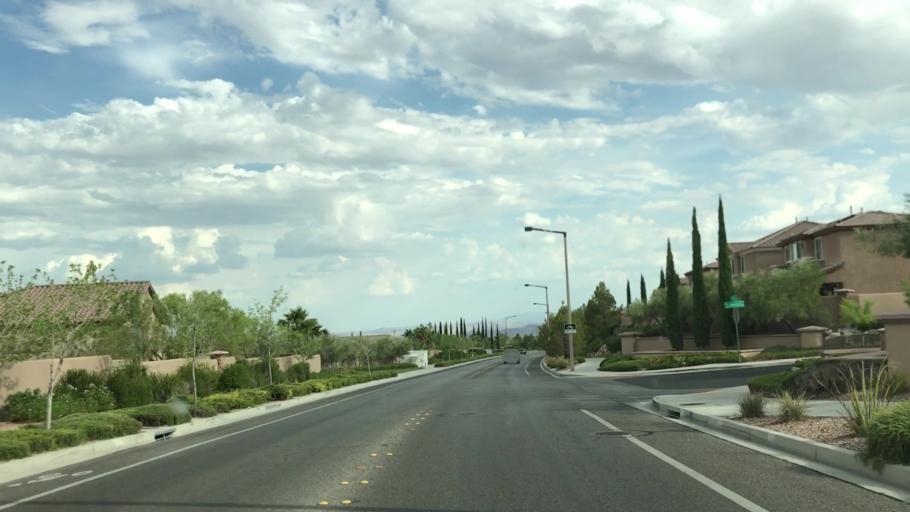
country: US
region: Nevada
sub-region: Clark County
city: Summerlin South
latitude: 36.1694
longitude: -115.3508
